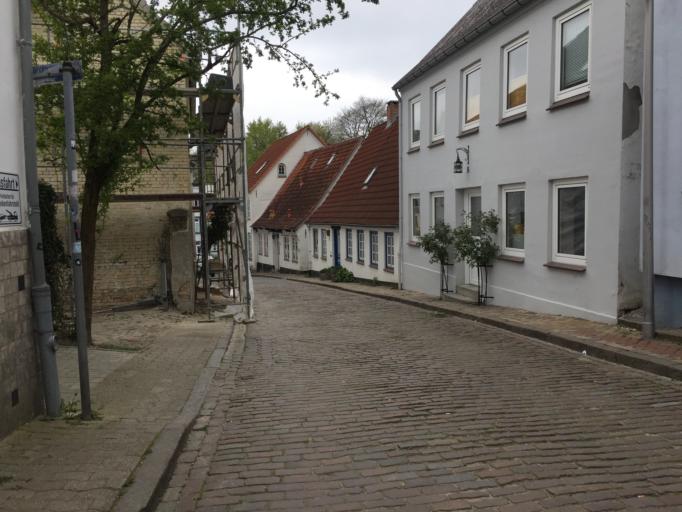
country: DE
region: Schleswig-Holstein
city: Flensburg
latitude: 54.7819
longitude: 9.4457
